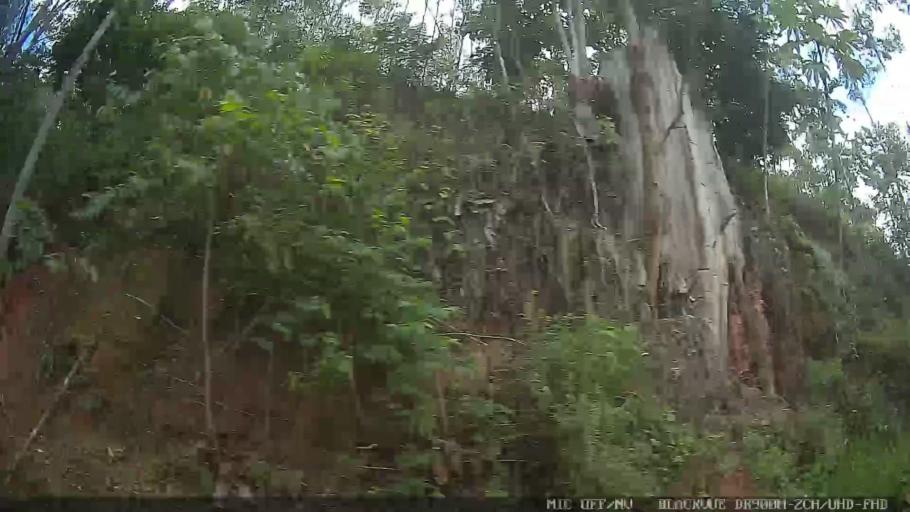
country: BR
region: Sao Paulo
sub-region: Caraguatatuba
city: Caraguatatuba
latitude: -23.5529
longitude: -45.6198
